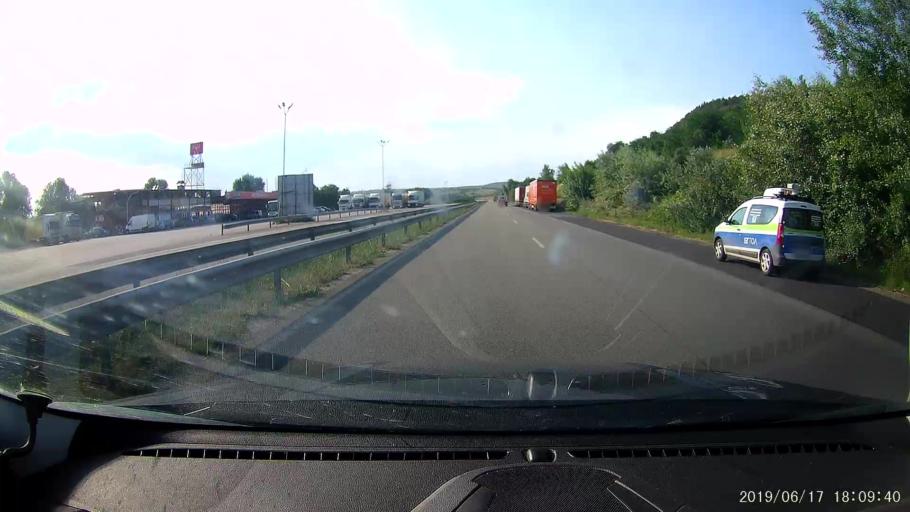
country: BG
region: Khaskovo
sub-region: Obshtina Lyubimets
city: Lyubimets
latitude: 41.8631
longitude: 26.0873
